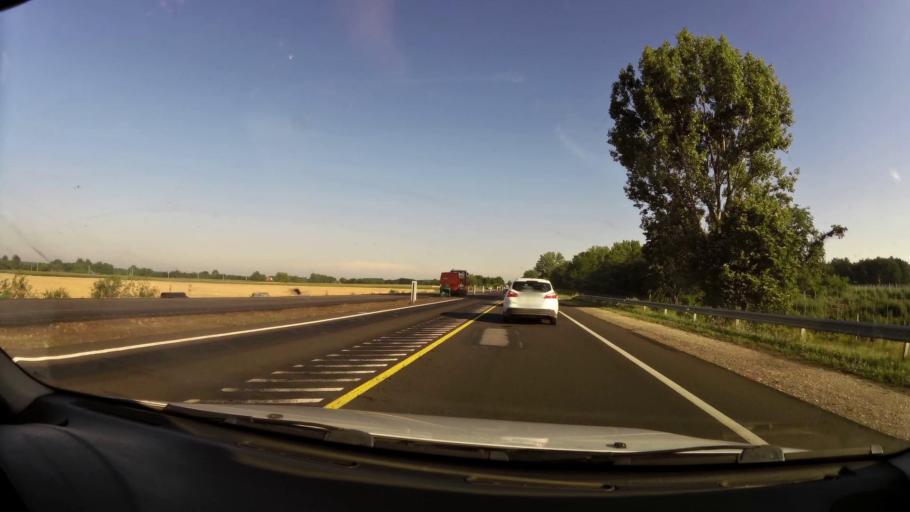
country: HU
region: Pest
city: Cegledbercel
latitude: 47.2428
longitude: 19.6556
